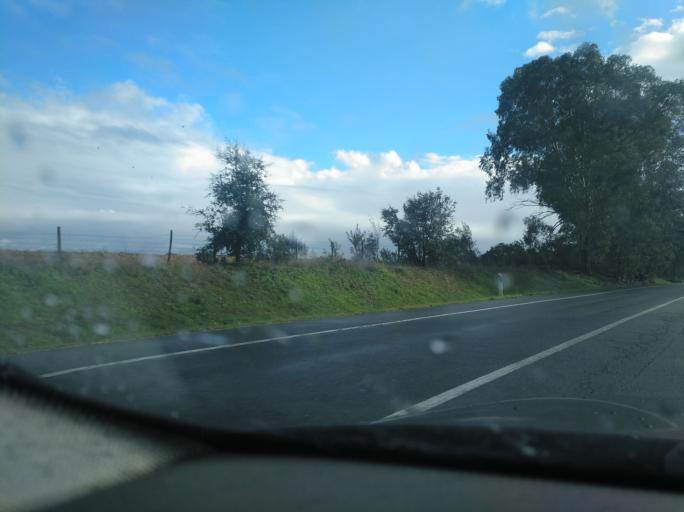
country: PT
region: Setubal
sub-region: Grandola
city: Grandola
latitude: 38.0340
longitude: -8.4004
